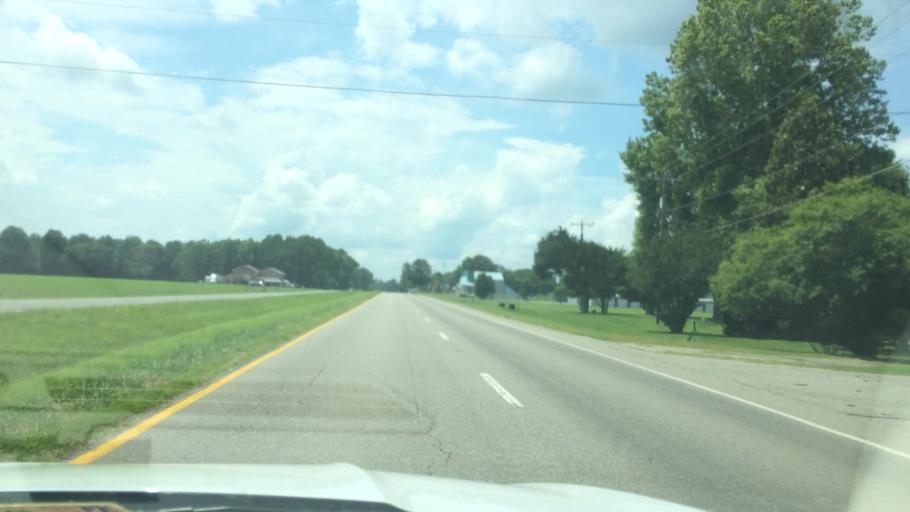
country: US
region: Virginia
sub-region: King William County
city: West Point
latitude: 37.5456
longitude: -76.7122
